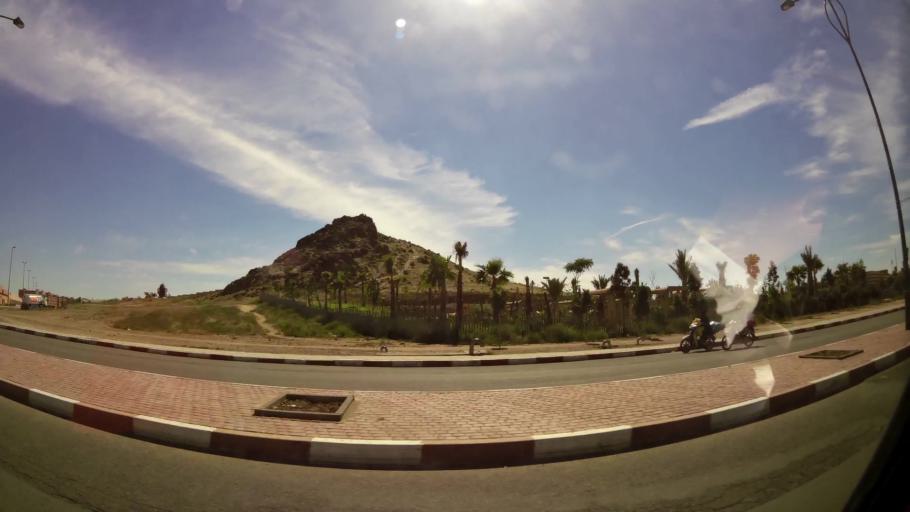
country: MA
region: Marrakech-Tensift-Al Haouz
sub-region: Marrakech
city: Marrakesh
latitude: 31.6711
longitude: -8.0138
